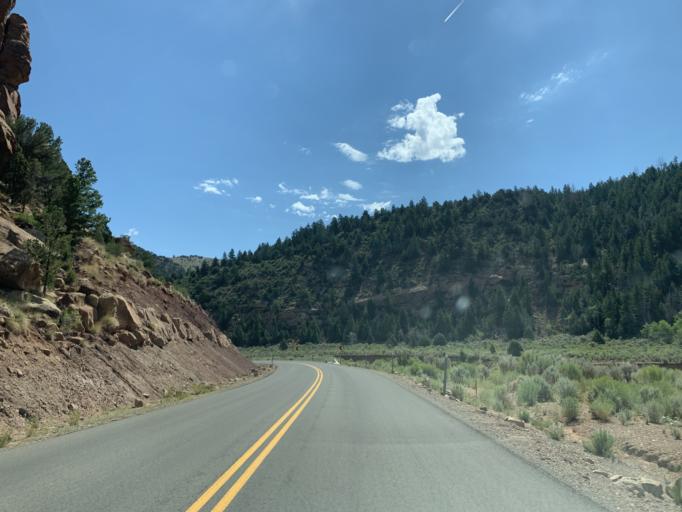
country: US
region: Utah
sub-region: Carbon County
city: East Carbon City
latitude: 39.7561
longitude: -110.5299
